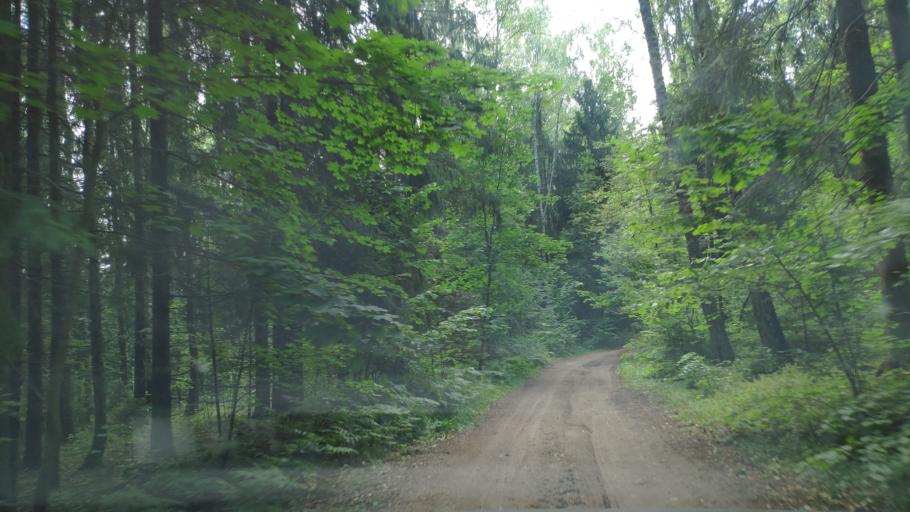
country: BY
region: Minsk
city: Khatsyezhyna
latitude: 53.9631
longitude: 27.2998
